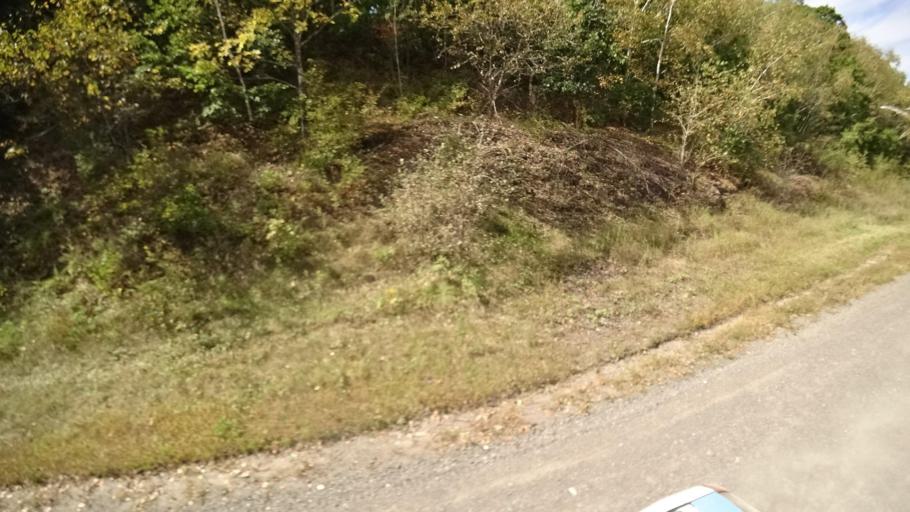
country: RU
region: Primorskiy
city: Yakovlevka
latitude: 44.7014
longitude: 133.6529
